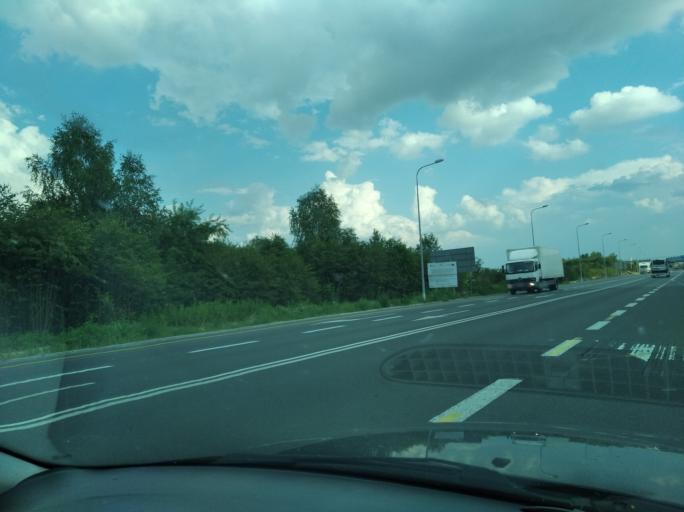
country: PL
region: Subcarpathian Voivodeship
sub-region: Powiat rzeszowski
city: Rudna Mala
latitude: 50.1121
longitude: 21.9739
